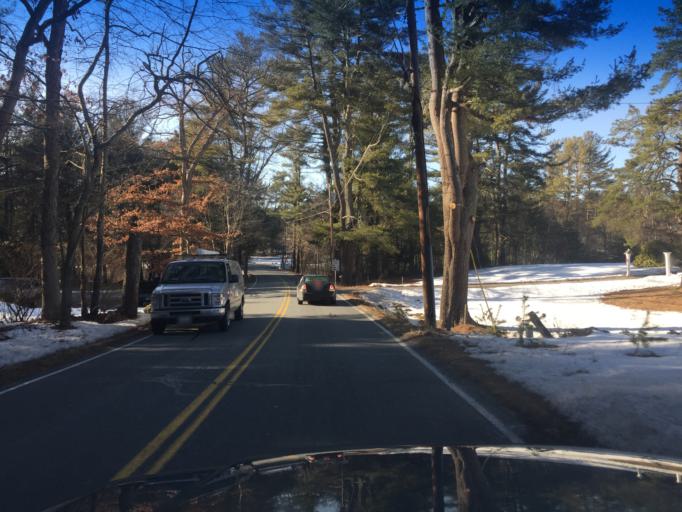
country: US
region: Massachusetts
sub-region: Norfolk County
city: Bellingham
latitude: 42.0908
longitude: -71.5110
